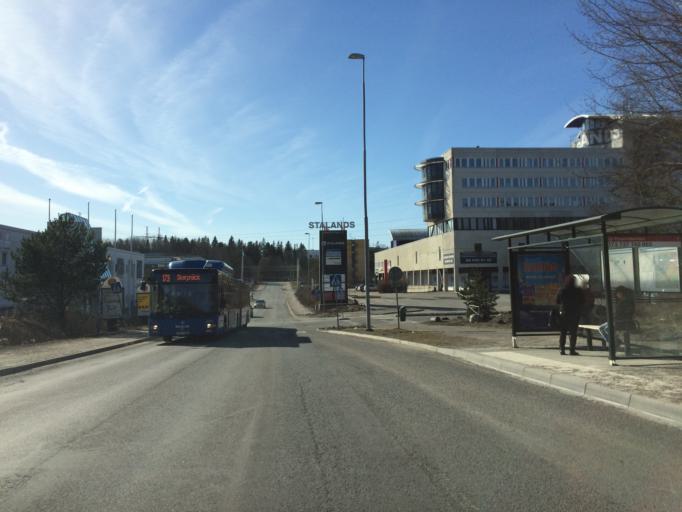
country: SE
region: Stockholm
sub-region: Huddinge Kommun
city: Segeltorp
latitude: 59.2647
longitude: 17.9061
